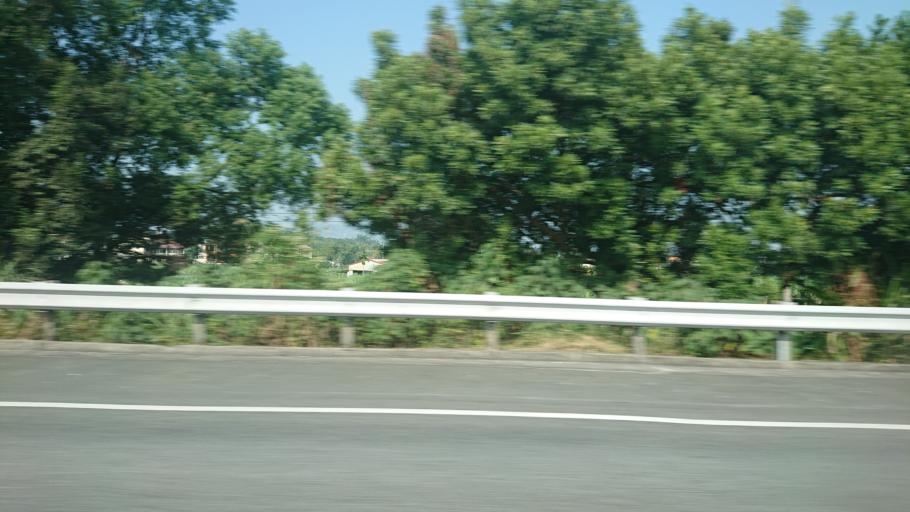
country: TW
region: Taiwan
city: Lugu
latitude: 23.7798
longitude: 120.7007
